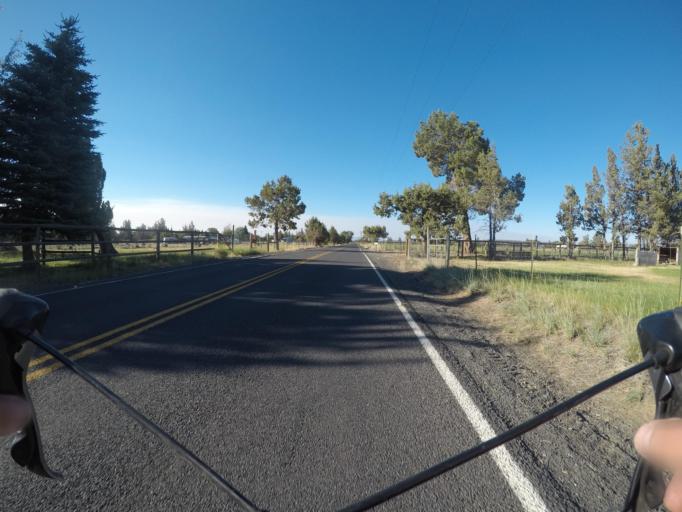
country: US
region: Oregon
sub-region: Deschutes County
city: Redmond
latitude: 44.2144
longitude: -121.2436
